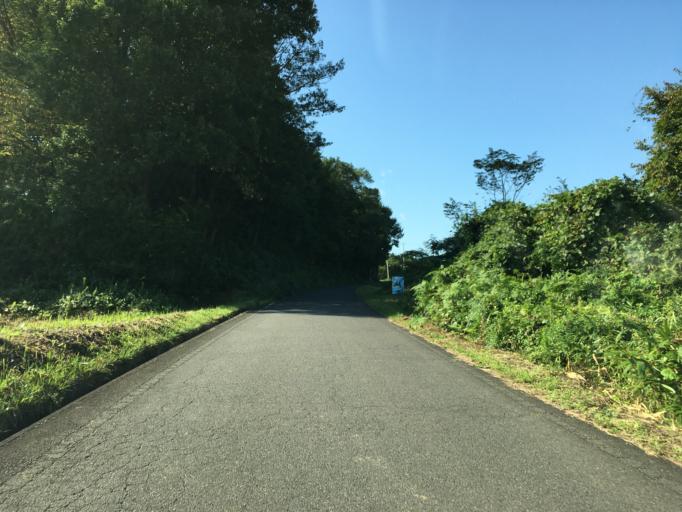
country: JP
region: Fukushima
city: Motomiya
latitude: 37.5533
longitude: 140.3692
